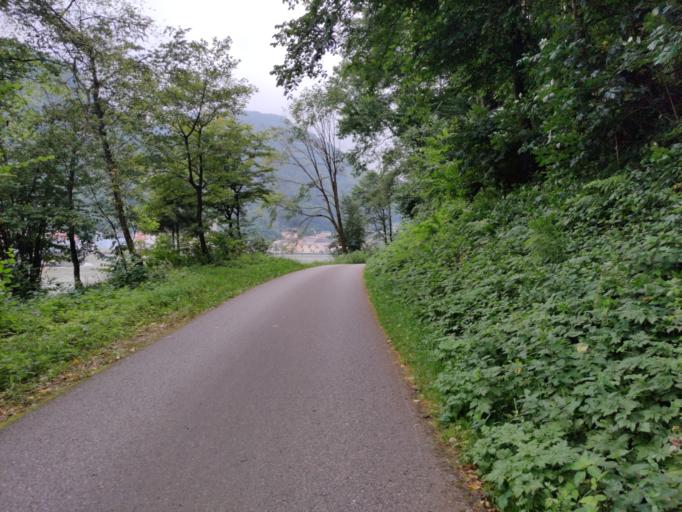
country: AT
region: Lower Austria
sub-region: Politischer Bezirk Melk
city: Nochling
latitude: 48.2309
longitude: 14.9330
